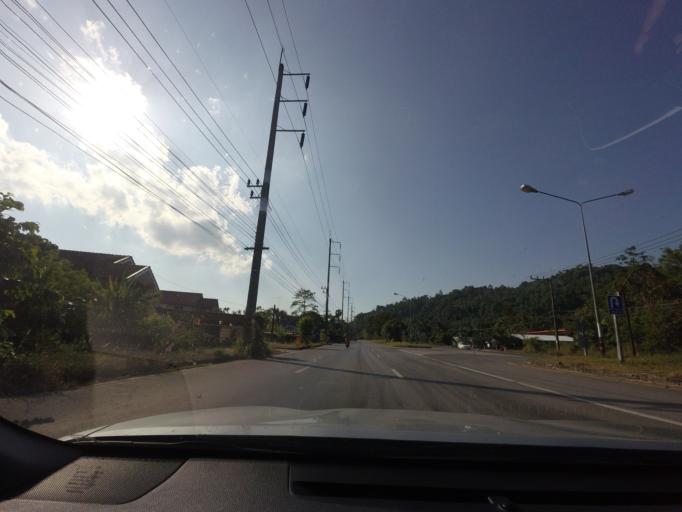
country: TH
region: Phangnga
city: Thai Mueang
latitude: 8.2715
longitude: 98.3281
